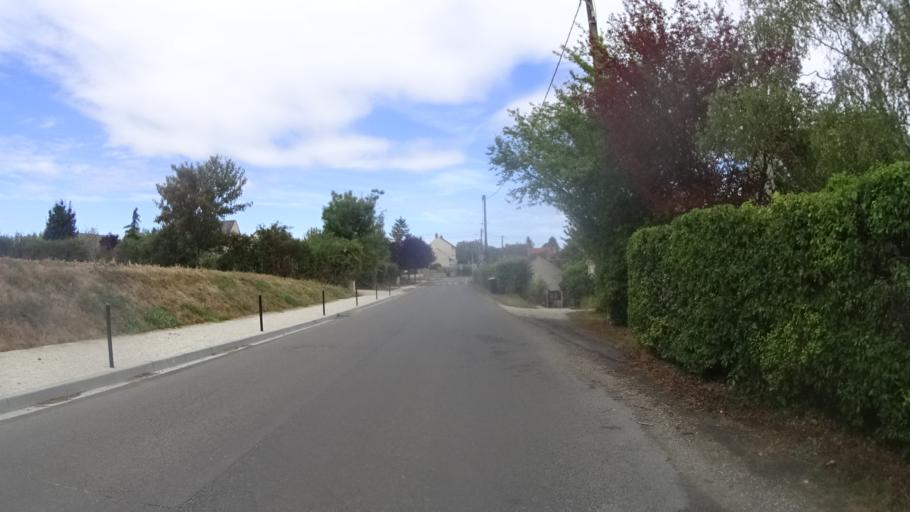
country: FR
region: Centre
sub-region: Departement du Loiret
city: Malesherbes
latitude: 48.2323
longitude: 2.4284
